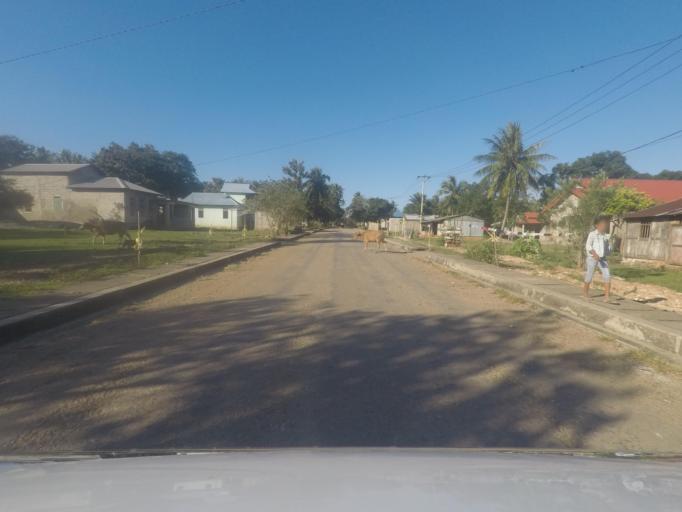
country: TL
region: Lautem
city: Lospalos
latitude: -8.4011
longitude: 127.1825
